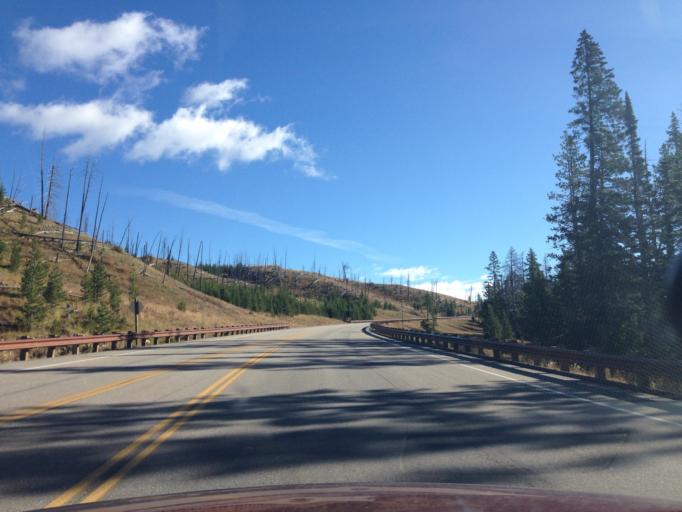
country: US
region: Montana
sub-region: Stillwater County
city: Absarokee
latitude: 45.0249
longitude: -109.9150
